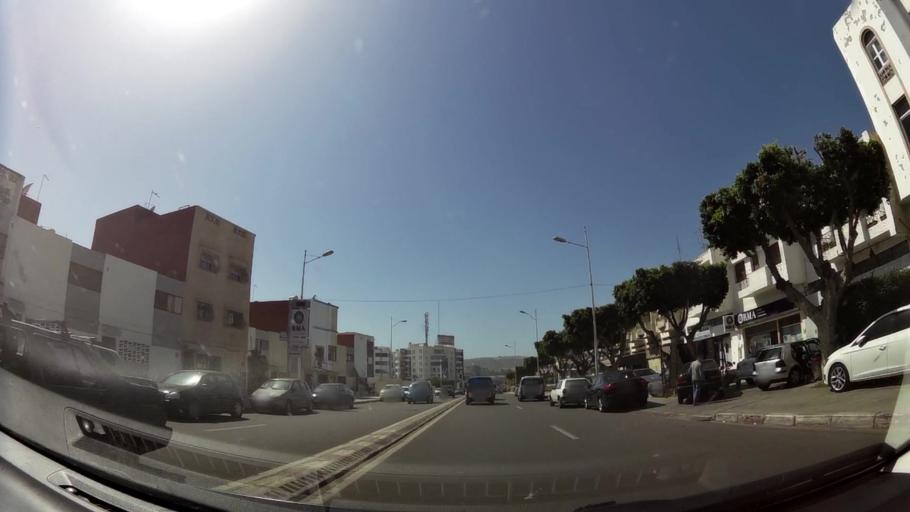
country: MA
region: Souss-Massa-Draa
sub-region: Agadir-Ida-ou-Tnan
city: Agadir
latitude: 30.4238
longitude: -9.5877
